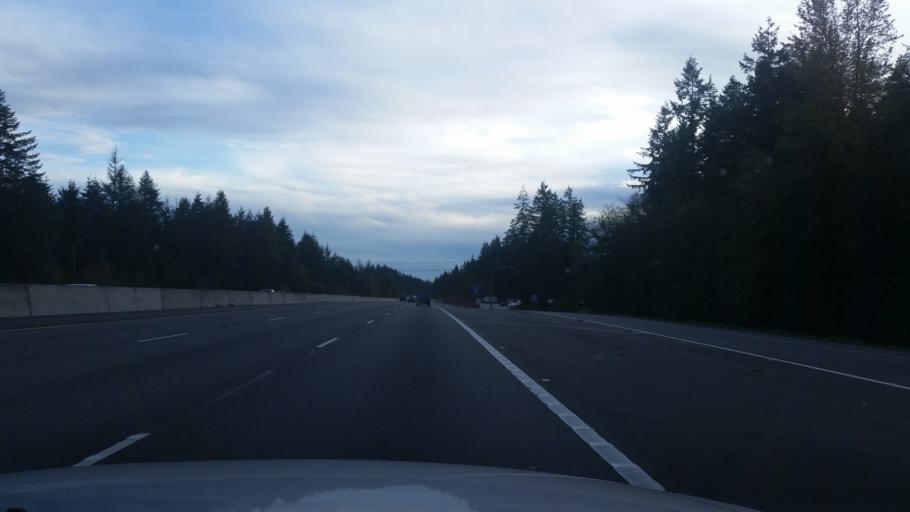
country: US
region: Washington
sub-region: Thurston County
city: Grand Mound
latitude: 46.8737
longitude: -122.9683
